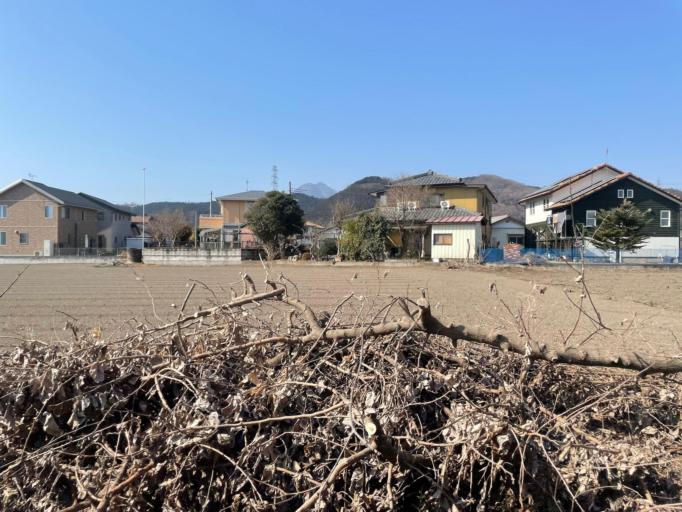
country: JP
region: Gunma
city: Shibukawa
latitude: 36.5129
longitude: 138.9968
